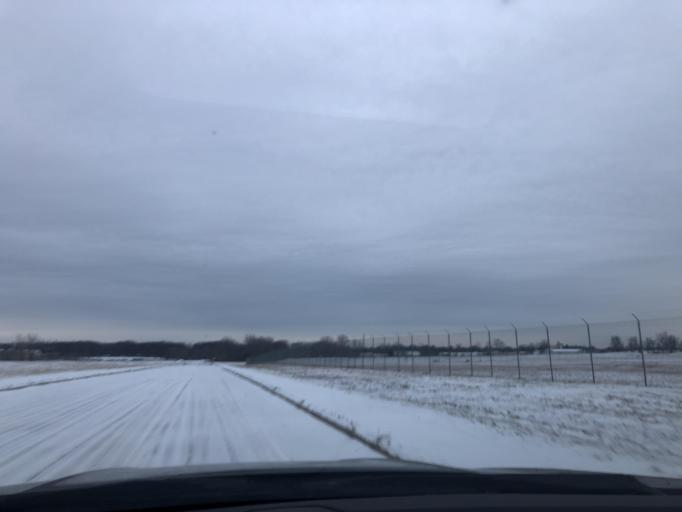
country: US
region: Michigan
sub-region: Ingham County
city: Edgemont Park
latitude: 42.7749
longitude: -84.5755
